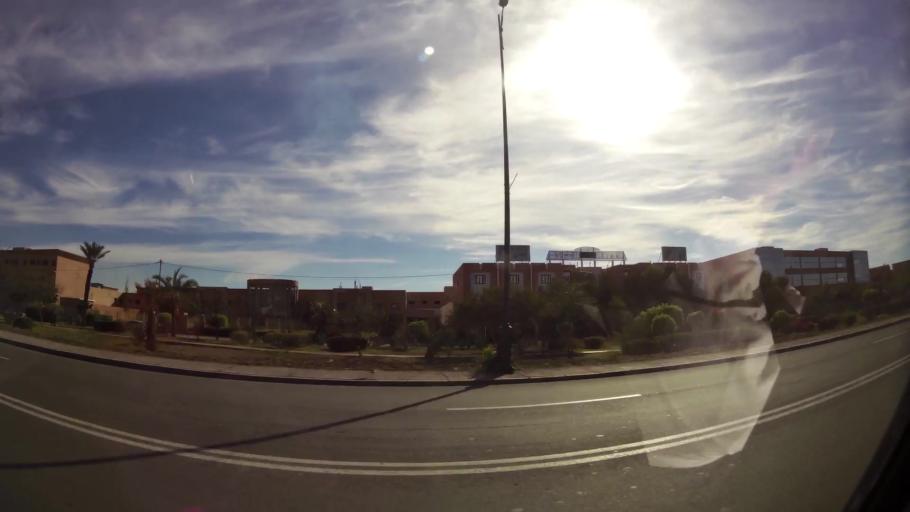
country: MA
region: Marrakech-Tensift-Al Haouz
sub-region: Marrakech
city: Marrakesh
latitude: 31.6752
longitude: -8.0444
